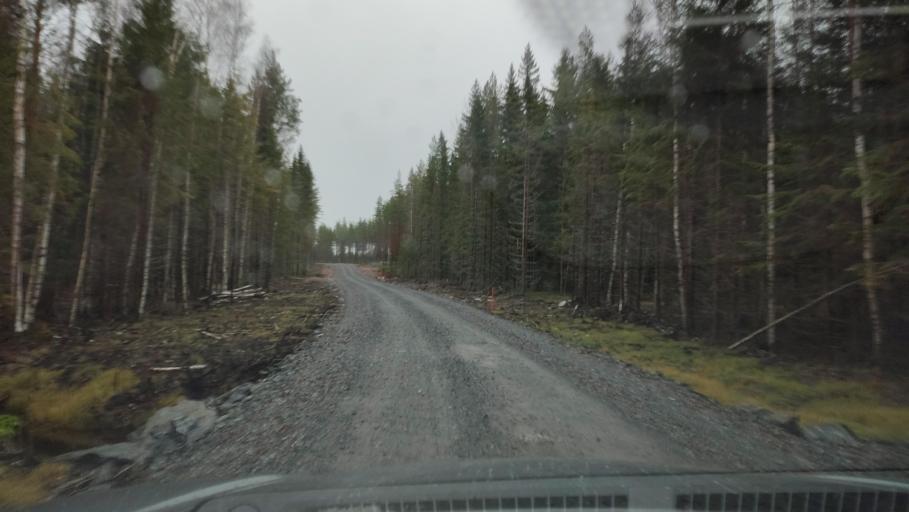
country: FI
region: Southern Ostrobothnia
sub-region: Suupohja
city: Karijoki
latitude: 62.1553
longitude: 21.6095
